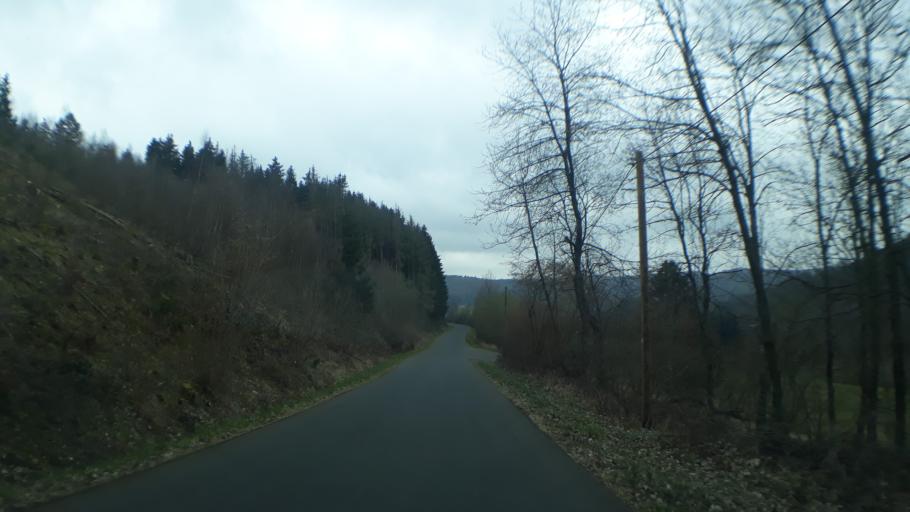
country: DE
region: North Rhine-Westphalia
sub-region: Regierungsbezirk Koln
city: Schleiden
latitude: 50.5410
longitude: 6.5004
